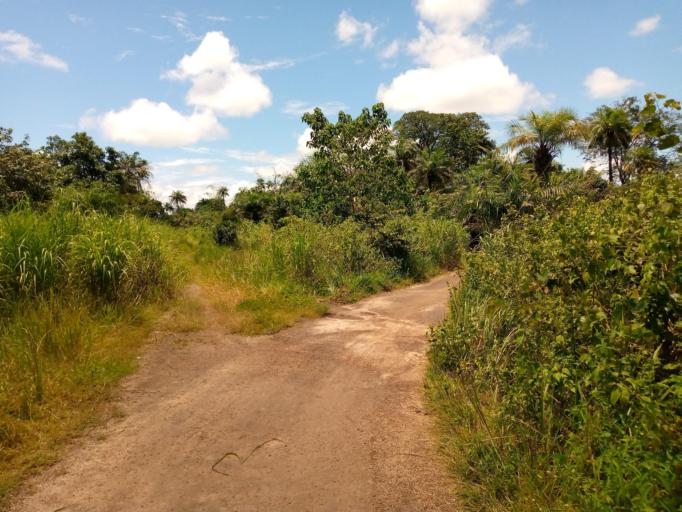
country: SL
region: Northern Province
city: Binkolo
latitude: 9.0591
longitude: -12.1515
